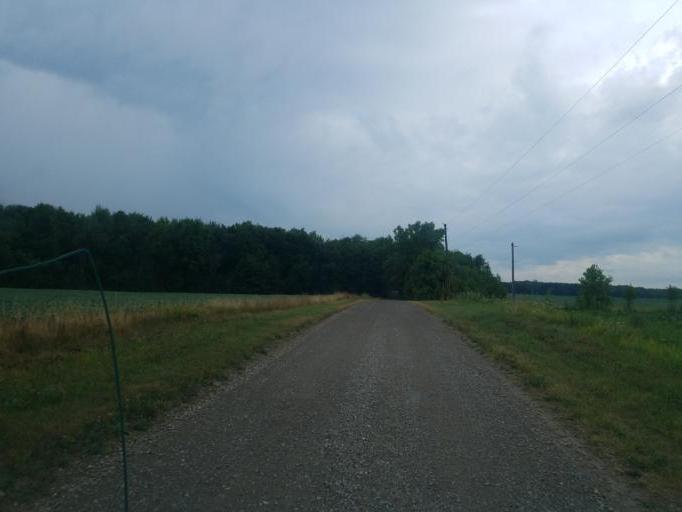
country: US
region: Ohio
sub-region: Defiance County
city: Hicksville
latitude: 41.3634
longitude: -84.8040
